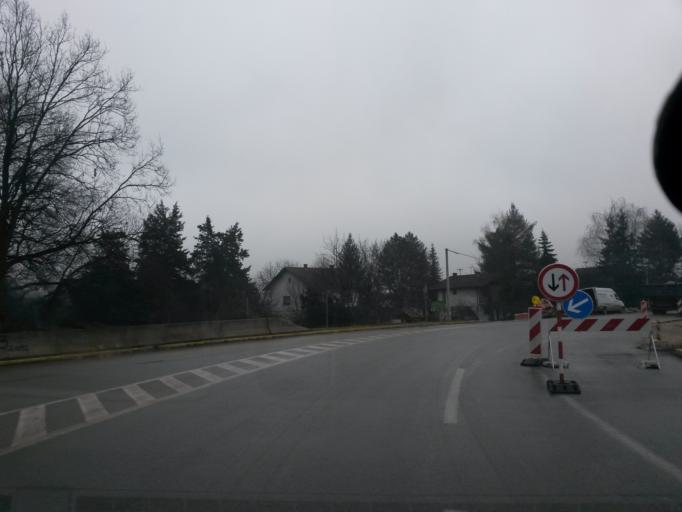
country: BA
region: Brcko
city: Brcko
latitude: 44.8875
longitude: 18.8160
